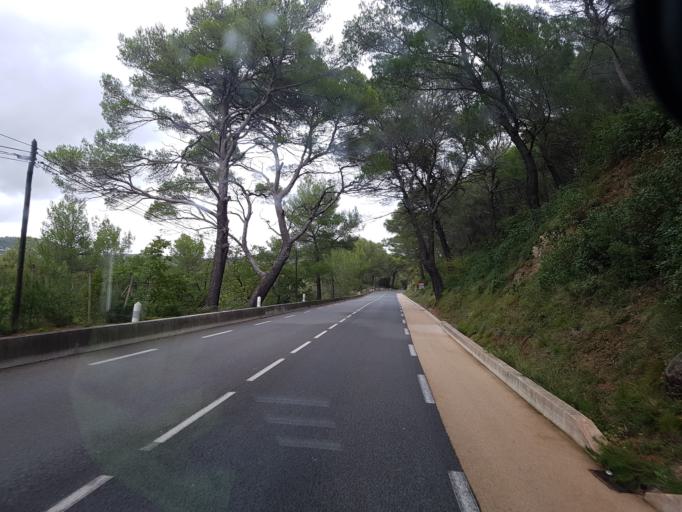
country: FR
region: Provence-Alpes-Cote d'Azur
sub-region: Departement des Bouches-du-Rhone
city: Cuges-les-Pins
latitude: 43.2674
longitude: 5.7337
